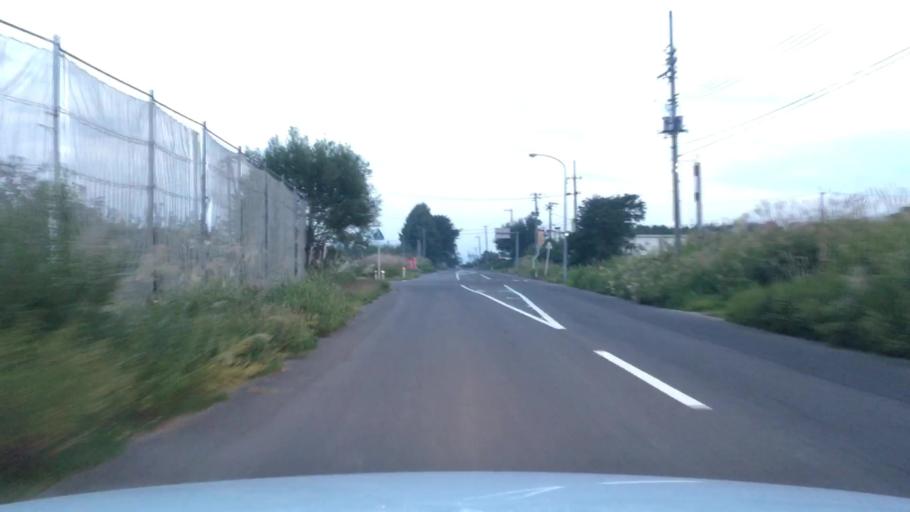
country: JP
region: Aomori
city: Hirosaki
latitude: 40.6785
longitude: 140.3732
